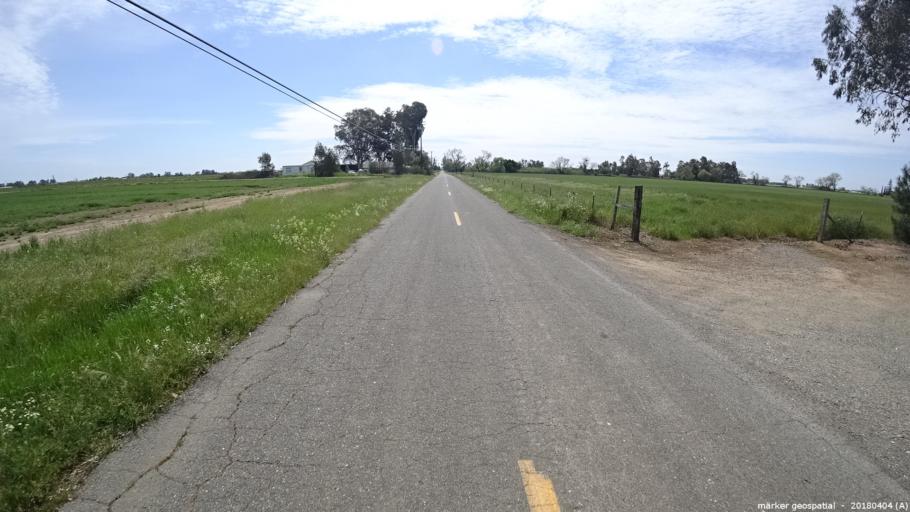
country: US
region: California
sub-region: Sacramento County
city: Herald
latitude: 38.2743
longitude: -121.2542
